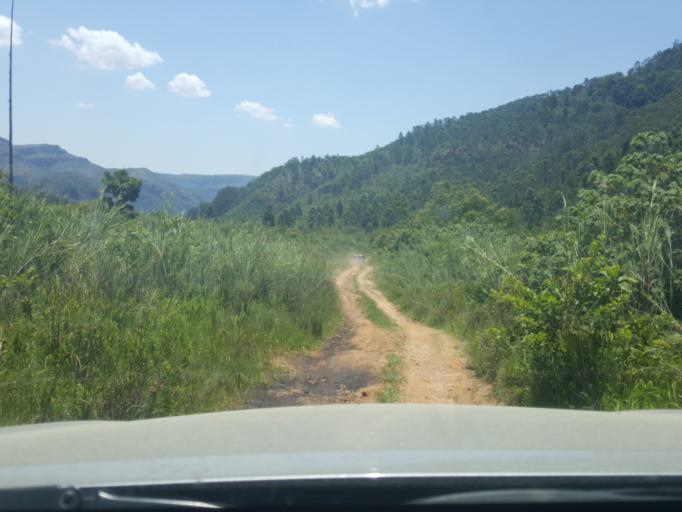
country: ZA
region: Limpopo
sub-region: Mopani District Municipality
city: Hoedspruit
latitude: -24.5949
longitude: 30.8631
